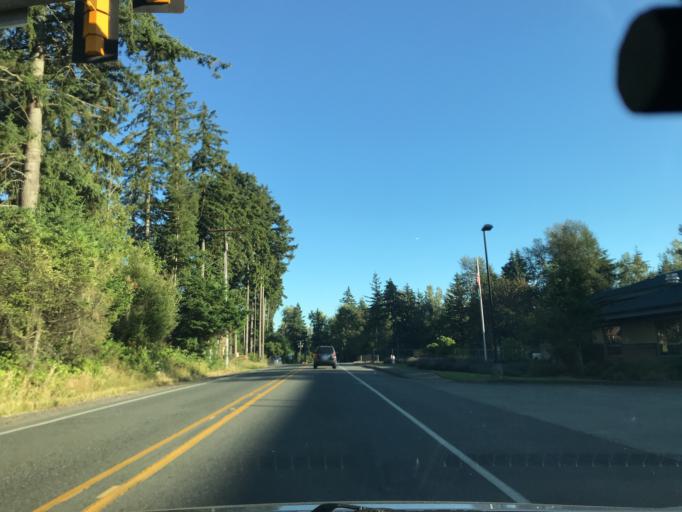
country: US
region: Washington
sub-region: King County
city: Pacific
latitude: 47.2539
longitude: -122.1869
